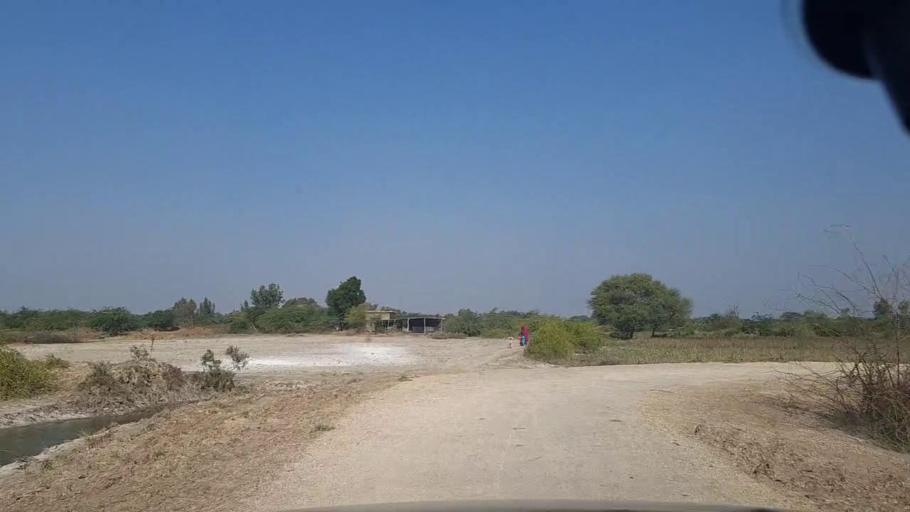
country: PK
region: Sindh
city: Chuhar Jamali
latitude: 24.5196
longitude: 67.8879
